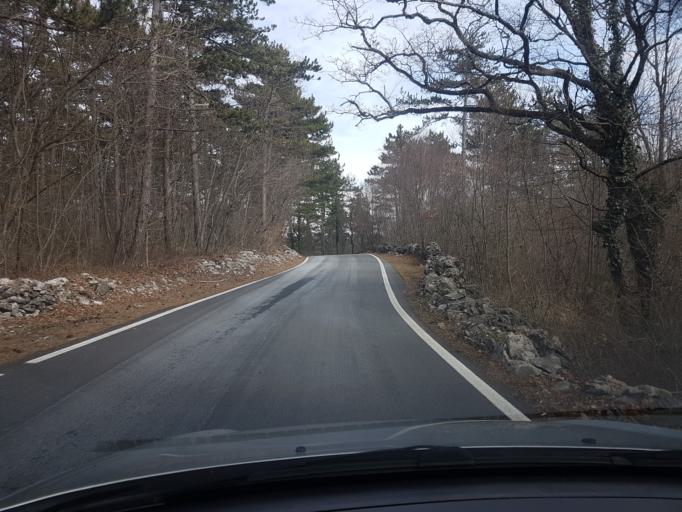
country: IT
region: Friuli Venezia Giulia
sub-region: Provincia di Trieste
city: Aurisina Cave
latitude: 45.7754
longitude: 13.6684
